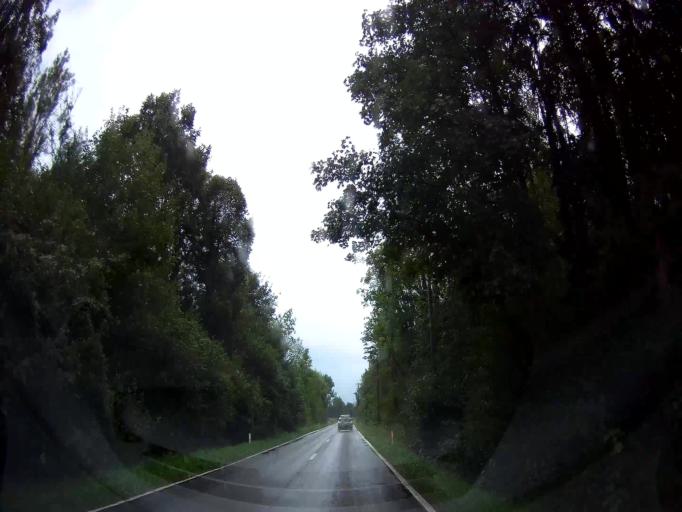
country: BE
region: Wallonia
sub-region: Province de Liege
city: Aywaille
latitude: 50.4556
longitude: 5.6381
